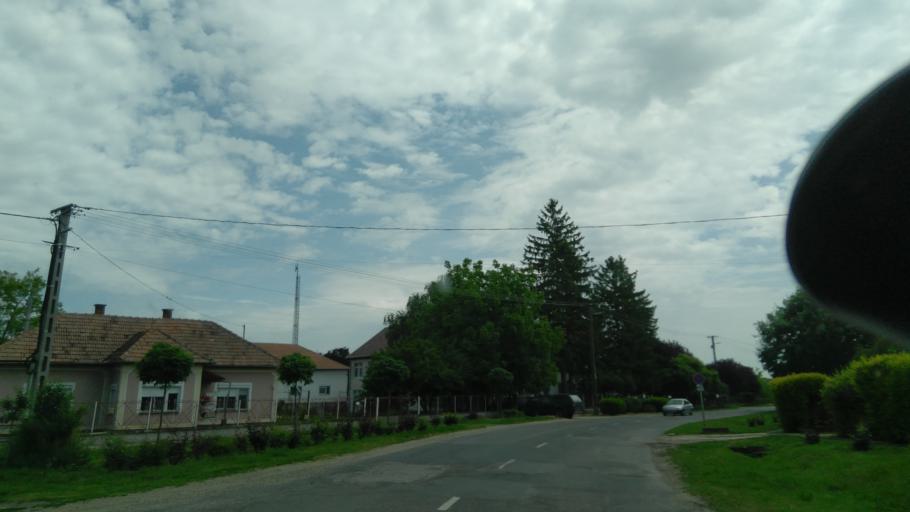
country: HU
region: Hajdu-Bihar
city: Komadi
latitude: 47.0227
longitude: 21.5435
